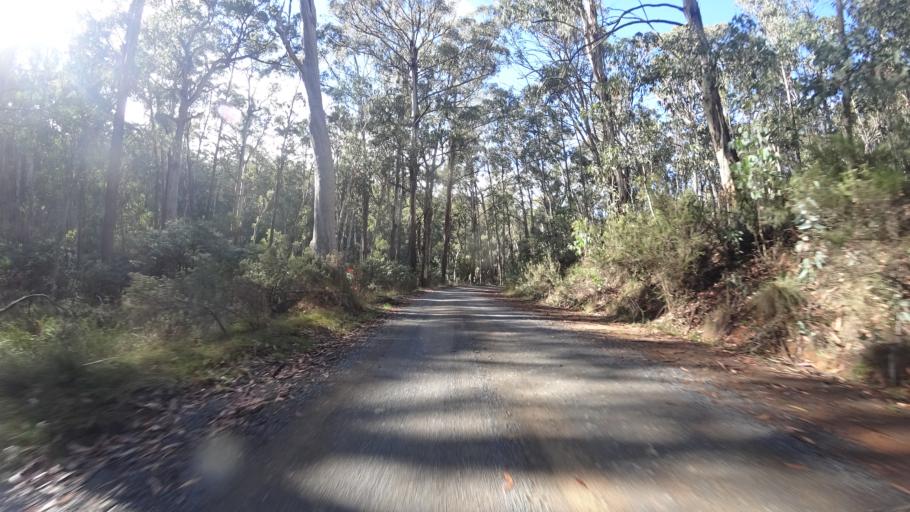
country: AU
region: New South Wales
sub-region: Tumut Shire
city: Tumut
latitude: -35.7128
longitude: 148.5048
